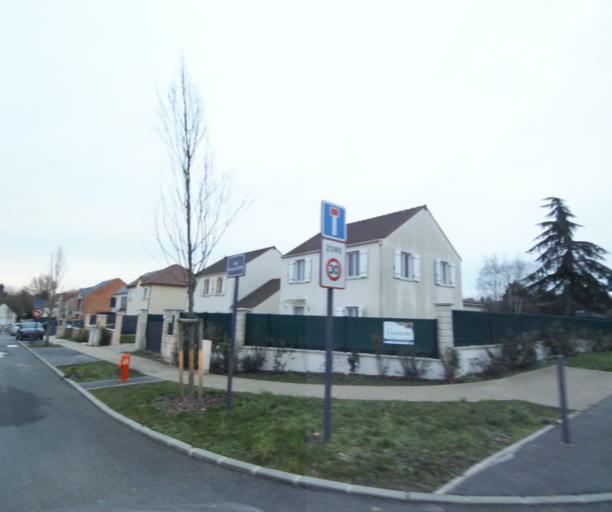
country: FR
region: Ile-de-France
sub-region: Departement de Seine-et-Marne
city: Dammartin-en-Goele
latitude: 49.0636
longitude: 2.6882
